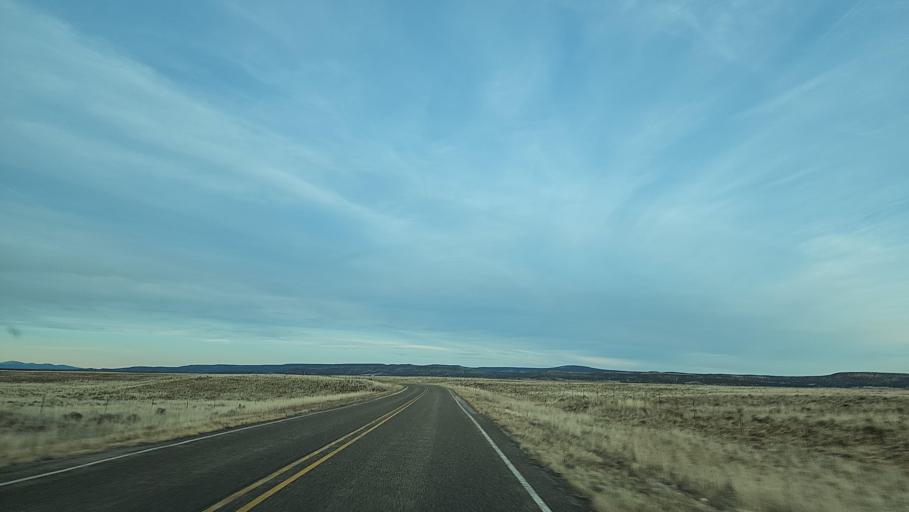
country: US
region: New Mexico
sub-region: Cibola County
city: Grants
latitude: 34.6884
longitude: -108.0606
